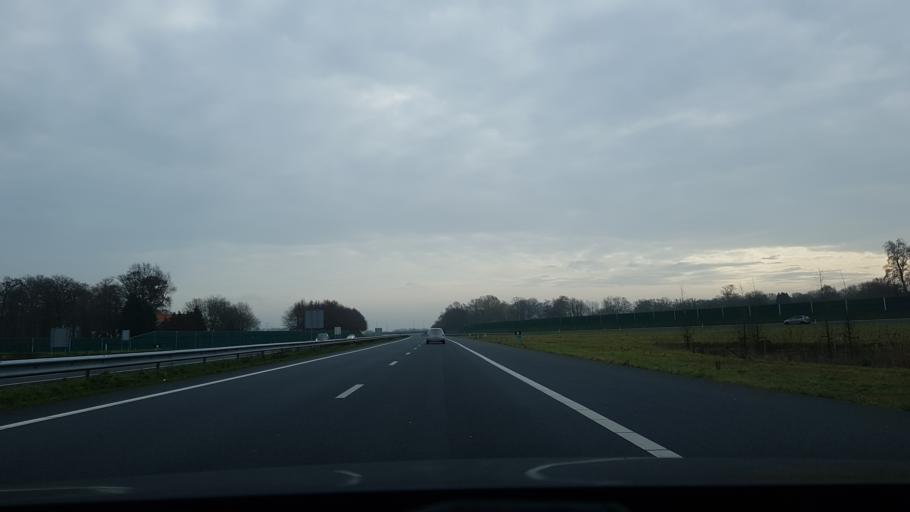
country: NL
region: Overijssel
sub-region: Gemeente Hengelo
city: Hengelo
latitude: 52.2063
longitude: 6.8265
